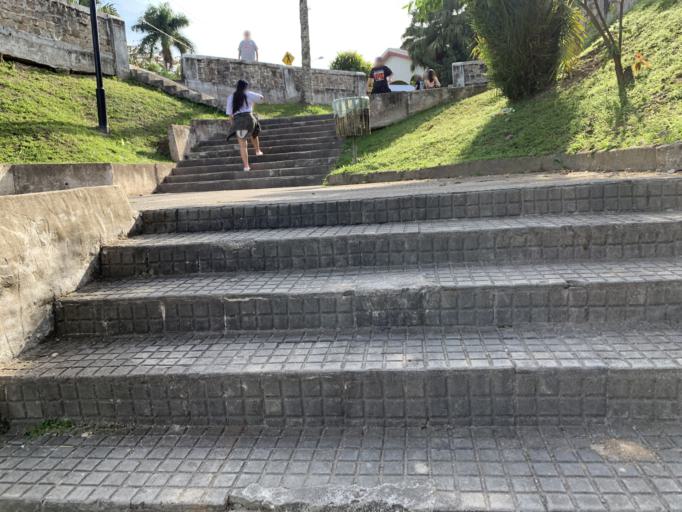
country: BR
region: Parana
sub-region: Antonina
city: Antonina
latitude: -25.4314
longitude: -48.7097
